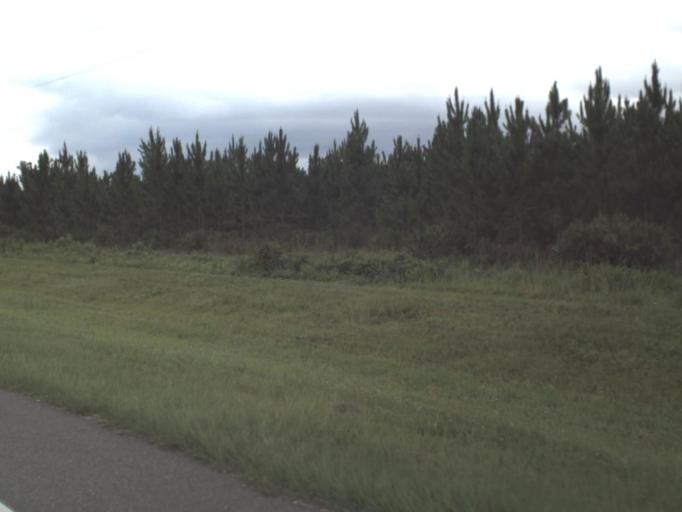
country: US
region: Florida
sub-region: Bradford County
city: Starke
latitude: 29.8656
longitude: -82.0753
